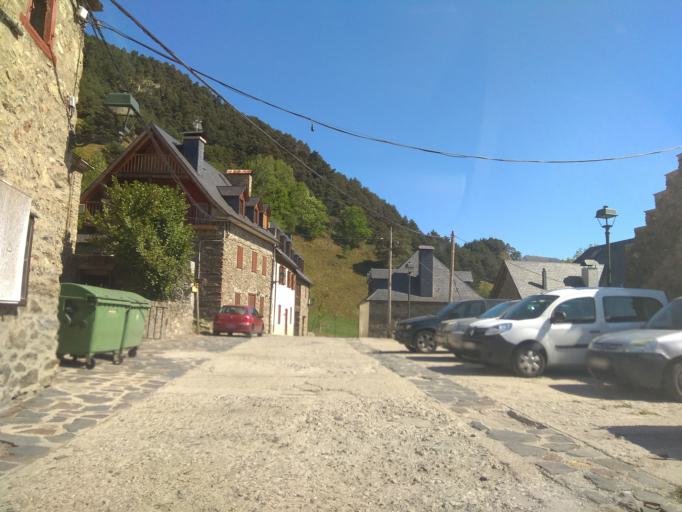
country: ES
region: Catalonia
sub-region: Provincia de Lleida
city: Les
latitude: 42.7571
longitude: 0.7123
